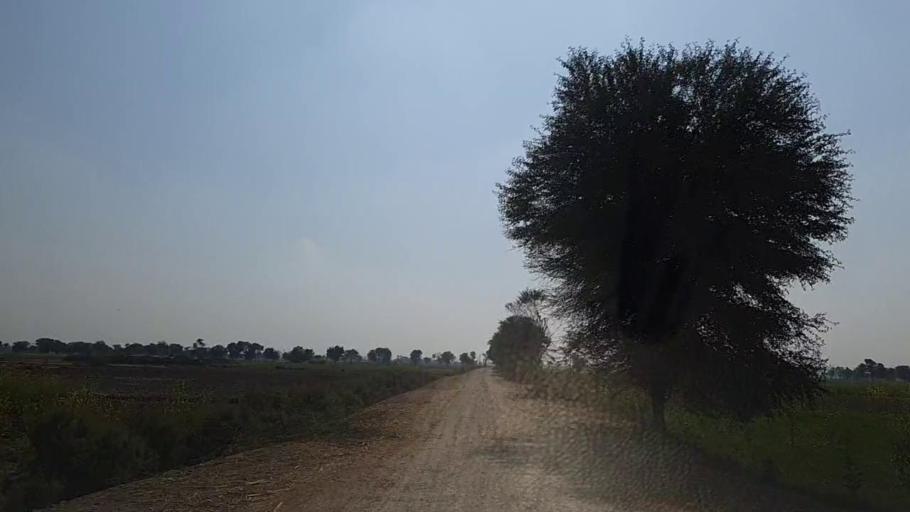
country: PK
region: Sindh
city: Daur
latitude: 26.4528
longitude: 68.2631
